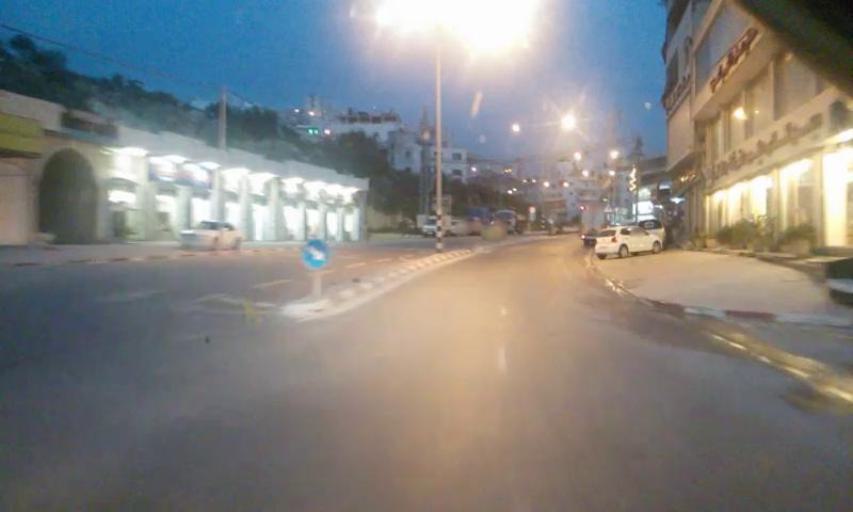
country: PS
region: West Bank
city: Zawata
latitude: 32.2409
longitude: 35.2277
